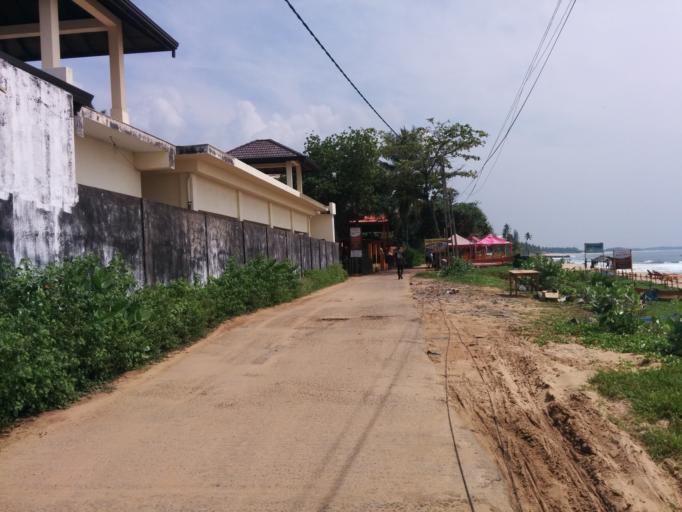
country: LK
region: Southern
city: Tangalla
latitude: 6.0361
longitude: 80.8040
